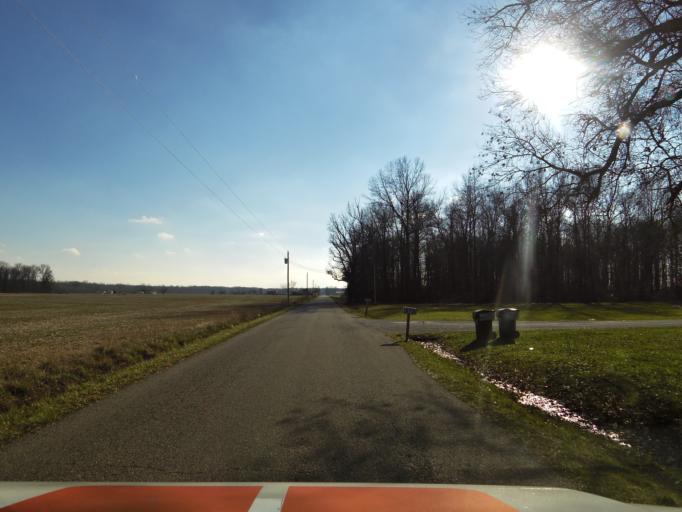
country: US
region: Indiana
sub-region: Jackson County
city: Seymour
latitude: 38.9885
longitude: -85.7975
